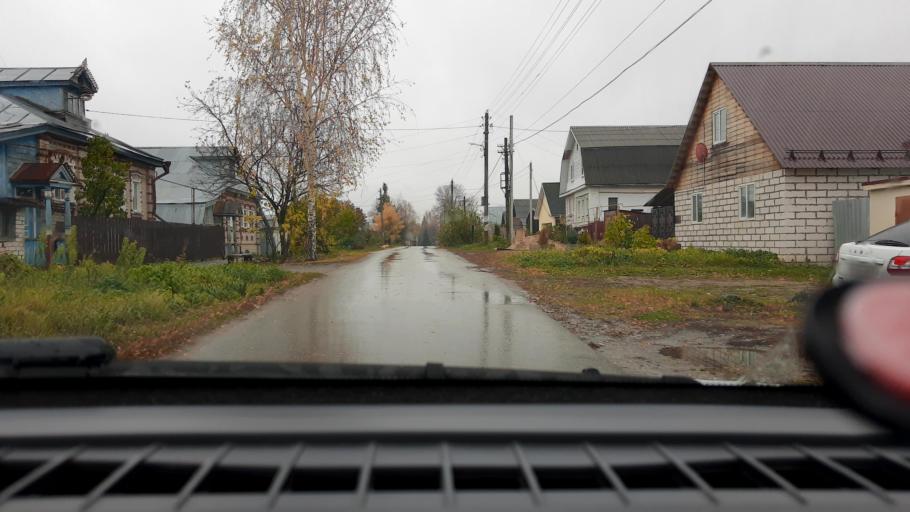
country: RU
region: Nizjnij Novgorod
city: Afonino
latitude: 56.2753
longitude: 44.1063
